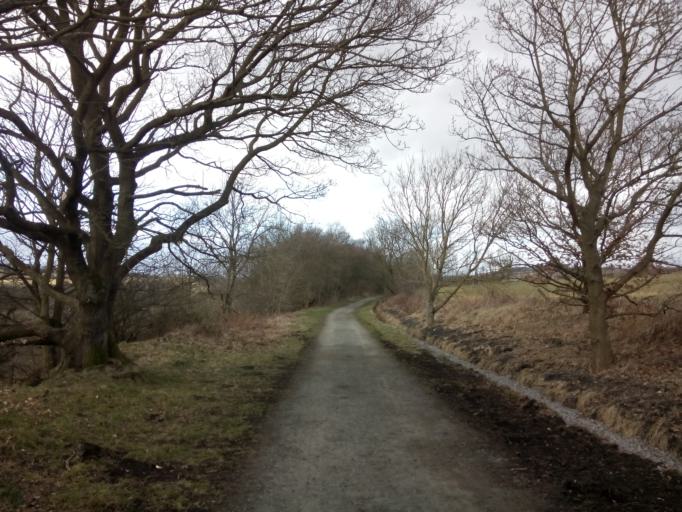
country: GB
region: England
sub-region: County Durham
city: Ushaw Moor
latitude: 54.7709
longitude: -1.6325
